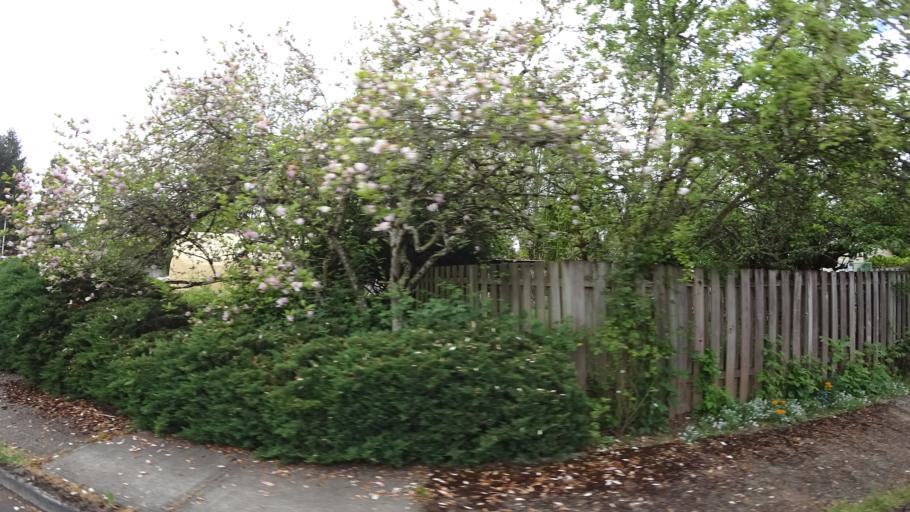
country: US
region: Oregon
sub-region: Washington County
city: Hillsboro
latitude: 45.4971
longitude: -122.9512
